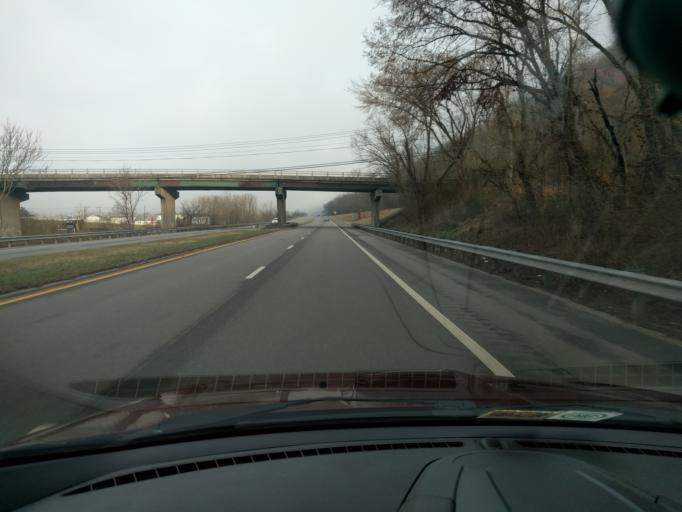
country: US
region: West Virginia
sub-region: Kanawha County
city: Chesapeake
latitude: 38.2247
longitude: -81.5284
